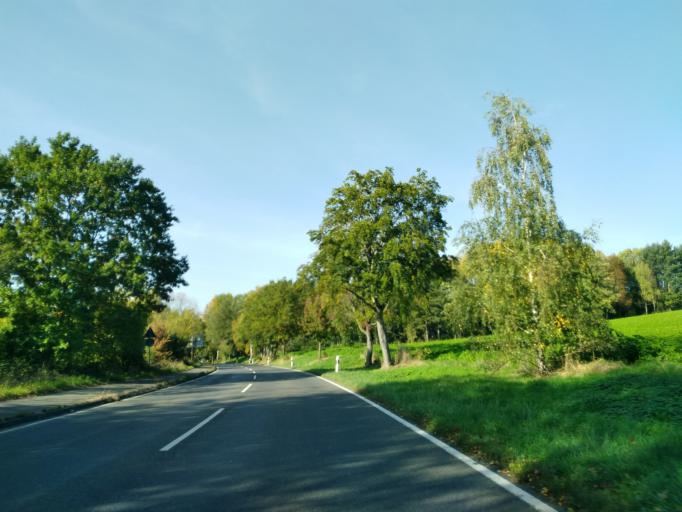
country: DE
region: North Rhine-Westphalia
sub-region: Regierungsbezirk Koln
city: Hennef
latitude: 50.7233
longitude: 7.2751
